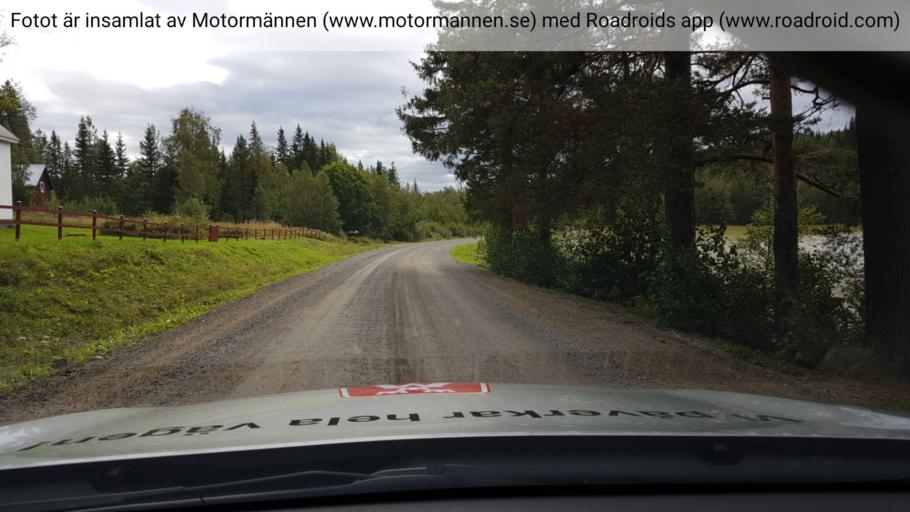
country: SE
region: Jaemtland
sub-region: Ragunda Kommun
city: Hammarstrand
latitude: 62.9533
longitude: 16.1145
